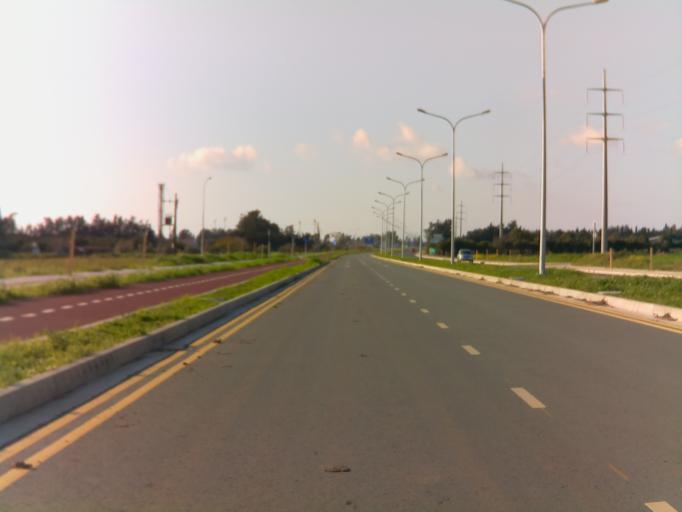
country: CY
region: Pafos
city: Paphos
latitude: 34.7372
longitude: 32.4567
